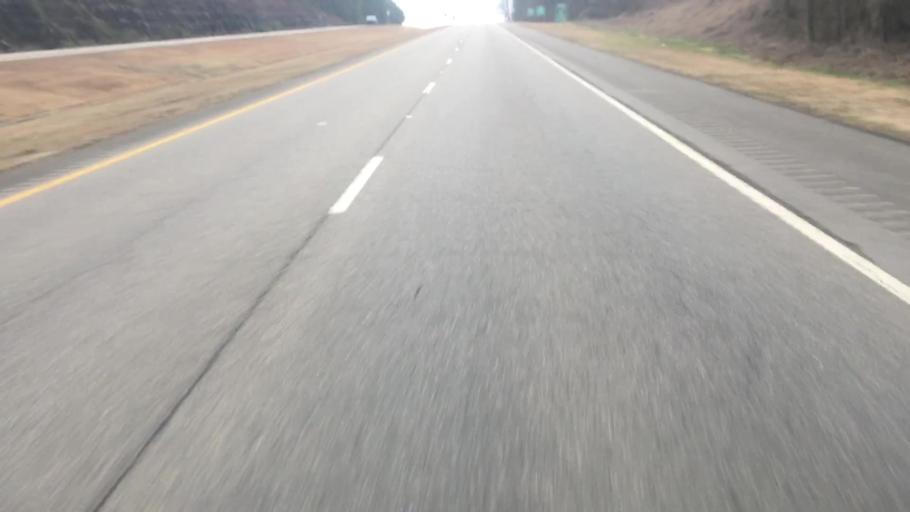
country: US
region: Alabama
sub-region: Walker County
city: Sumiton
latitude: 33.7679
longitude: -87.0711
